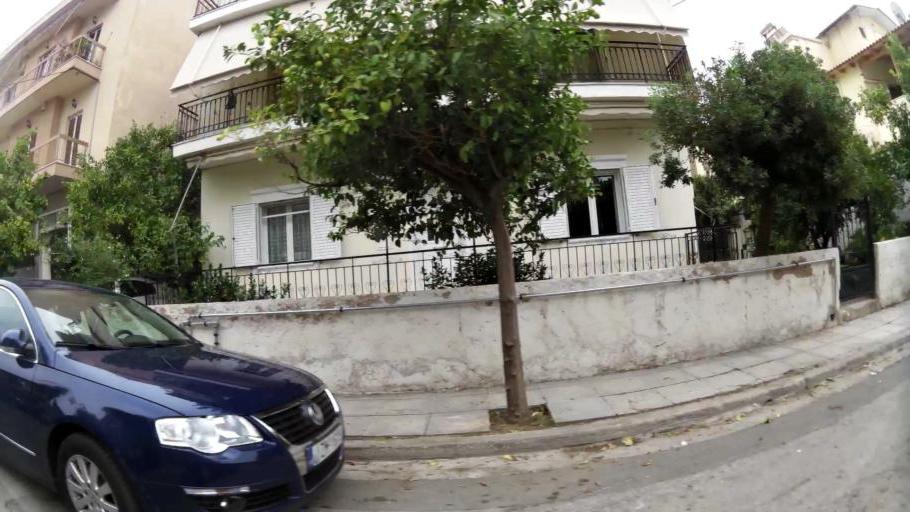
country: GR
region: Attica
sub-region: Nomarchia Athinas
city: Ilion
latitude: 38.0291
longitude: 23.7090
